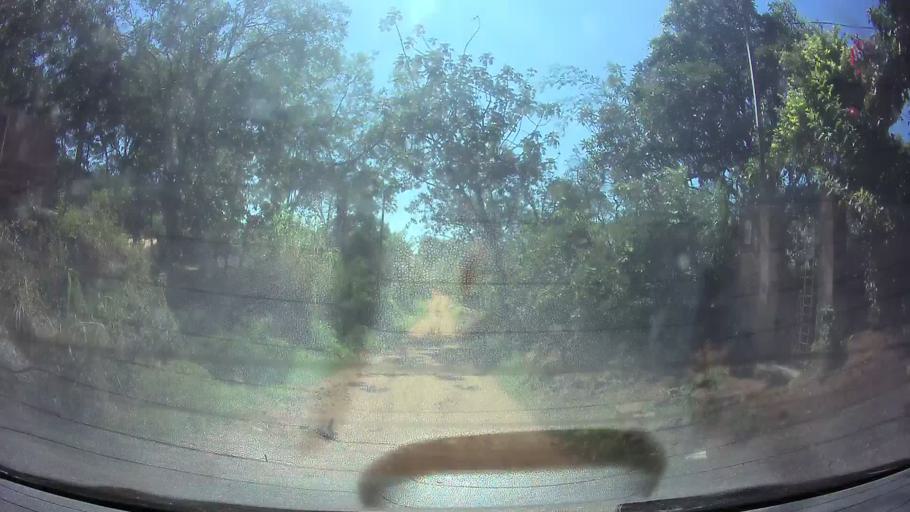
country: PY
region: Central
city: Limpio
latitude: -25.2436
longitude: -57.4450
